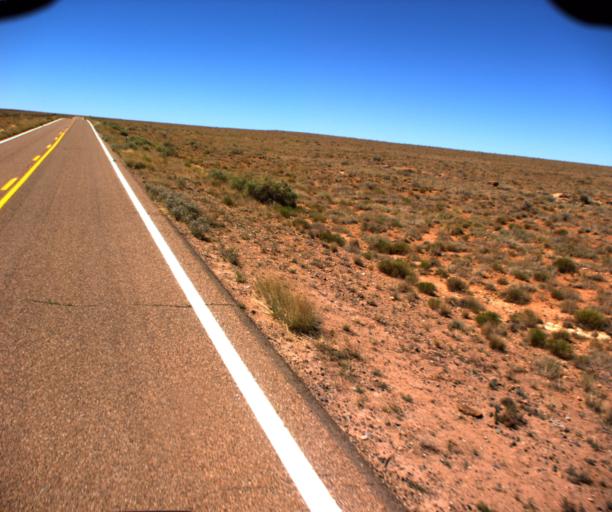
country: US
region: Arizona
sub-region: Navajo County
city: Winslow
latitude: 34.9226
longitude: -110.6378
